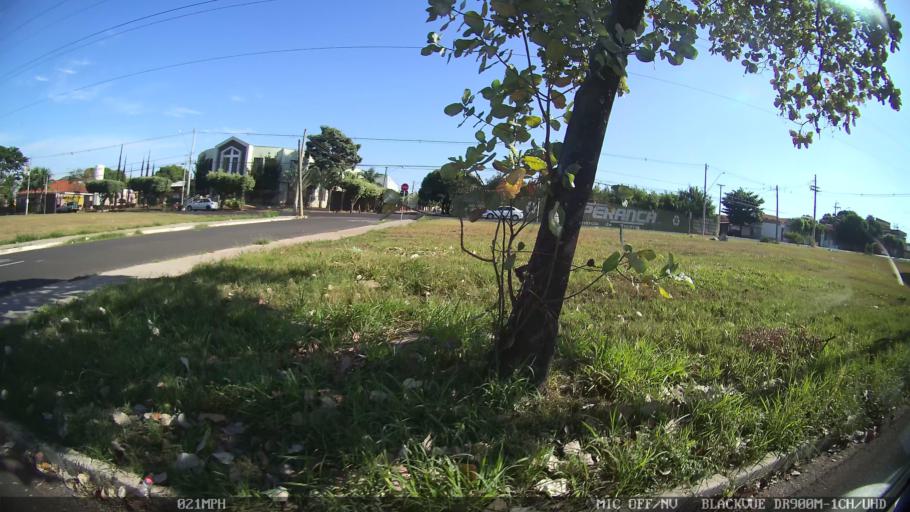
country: BR
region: Sao Paulo
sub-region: Sao Jose Do Rio Preto
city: Sao Jose do Rio Preto
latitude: -20.7833
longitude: -49.4073
